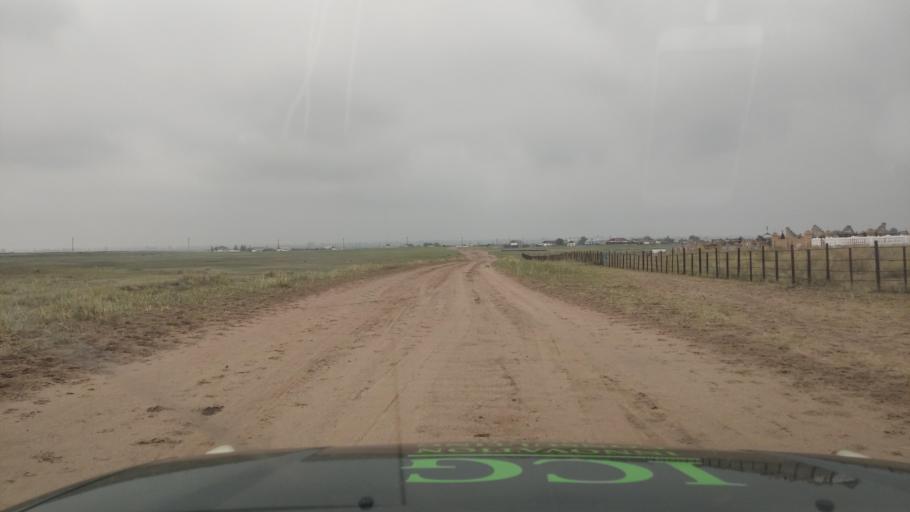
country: KZ
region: Pavlodar
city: Aksu
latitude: 52.0558
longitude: 77.1453
